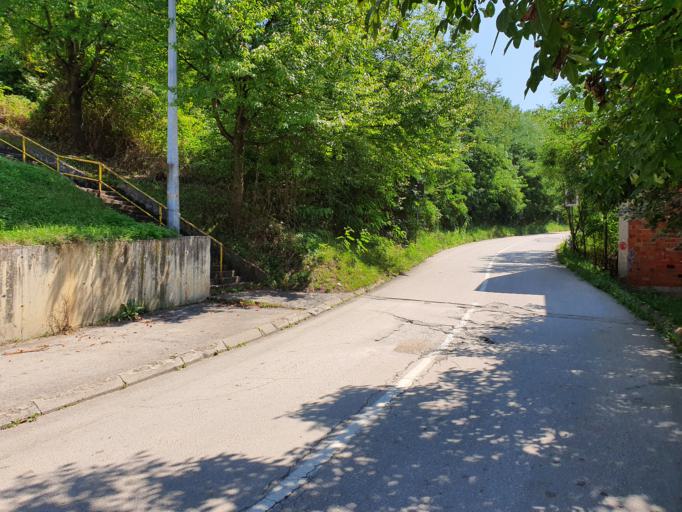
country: RS
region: Central Serbia
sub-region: Zlatiborski Okrug
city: Uzice
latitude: 43.8531
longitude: 19.8603
